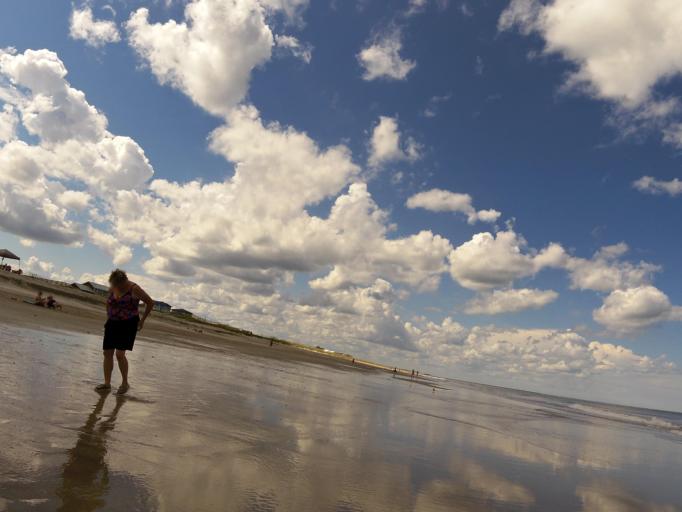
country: US
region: Florida
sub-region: Nassau County
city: Fernandina Beach
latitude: 30.6826
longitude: -81.4276
